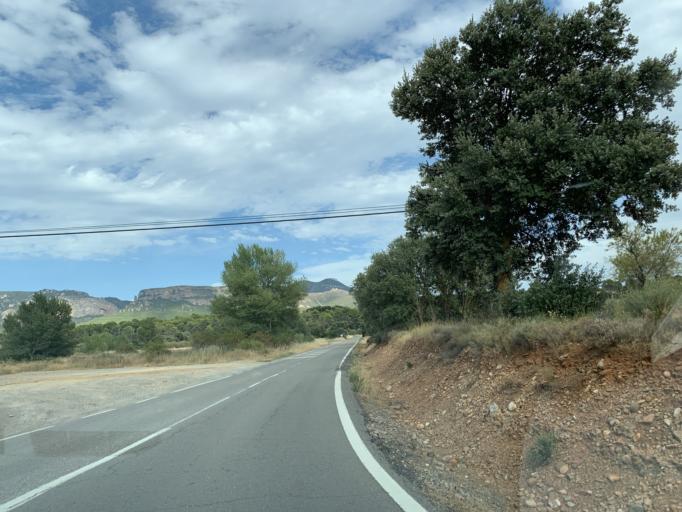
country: ES
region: Aragon
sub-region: Provincia de Zaragoza
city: Santa Eulalia de Gallego
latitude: 42.3140
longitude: -0.7524
